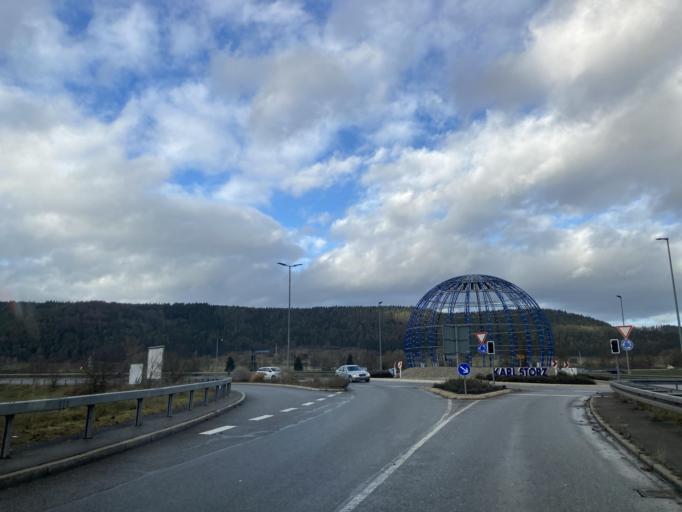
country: DE
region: Baden-Wuerttemberg
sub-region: Freiburg Region
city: Tuttlingen
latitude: 48.0009
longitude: 8.8294
